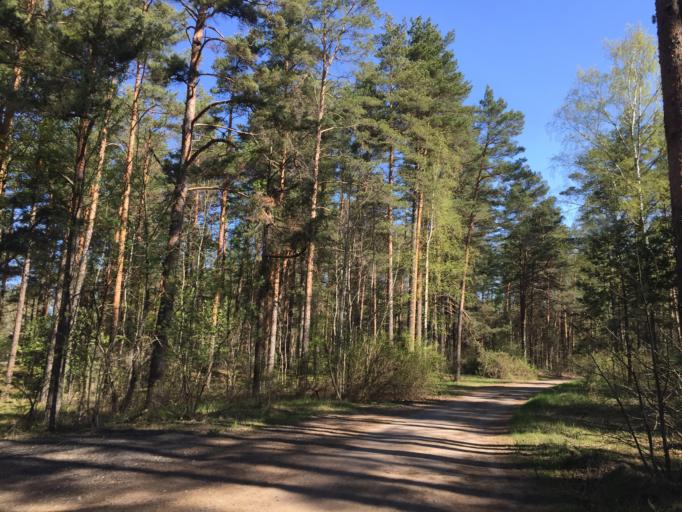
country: LV
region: Adazi
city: Adazi
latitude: 57.0906
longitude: 24.3403
